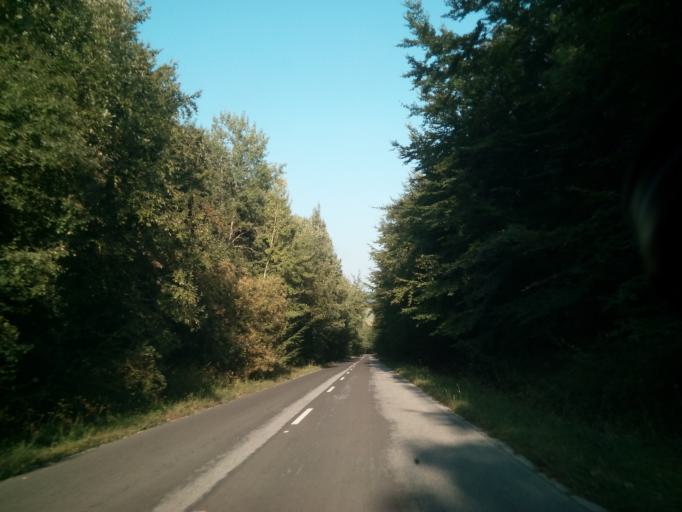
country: SK
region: Kosicky
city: Kosice
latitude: 48.7258
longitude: 21.1327
